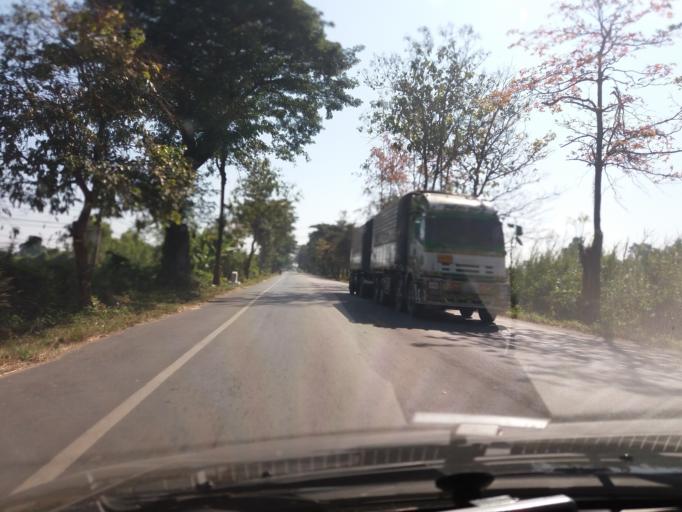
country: TH
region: Kamphaeng Phet
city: Khlong Khlung
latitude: 16.2078
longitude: 99.7487
